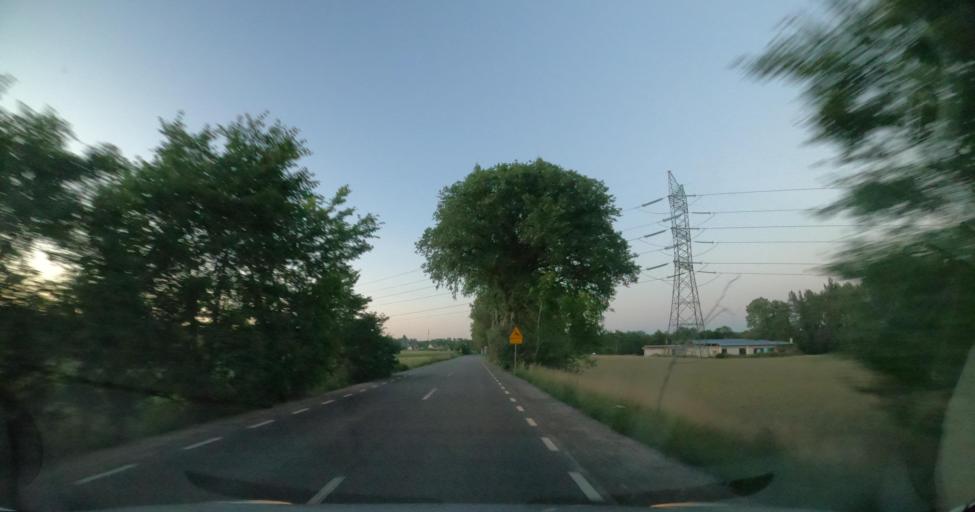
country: PL
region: Pomeranian Voivodeship
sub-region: Powiat wejherowski
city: Szemud
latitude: 54.4733
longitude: 18.1740
